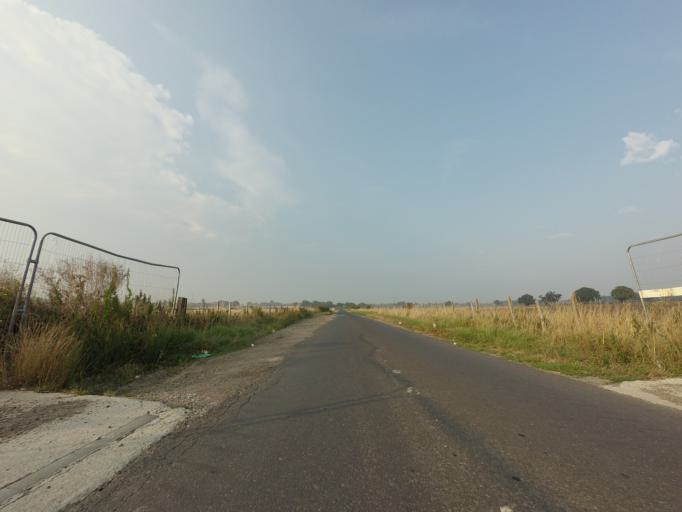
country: GB
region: England
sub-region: Kent
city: Ashford
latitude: 51.1218
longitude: 0.8259
